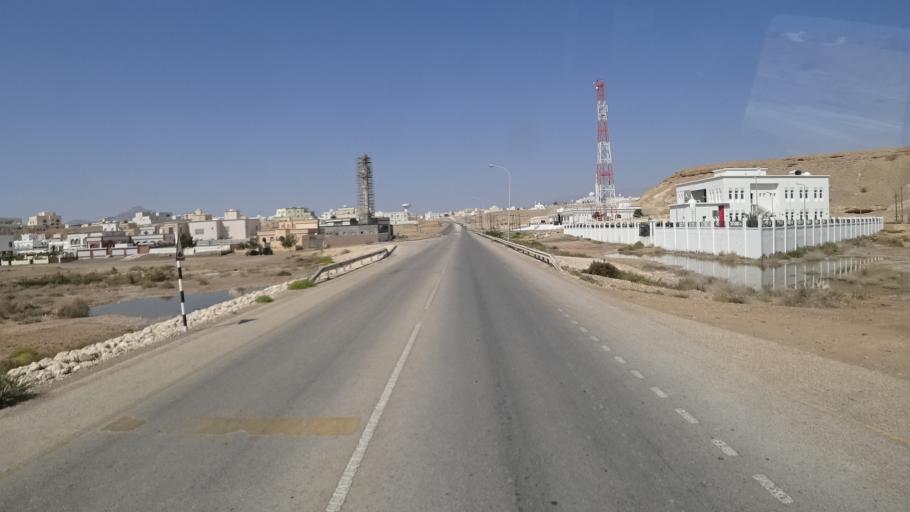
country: OM
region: Ash Sharqiyah
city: Sur
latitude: 22.5612
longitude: 59.5050
